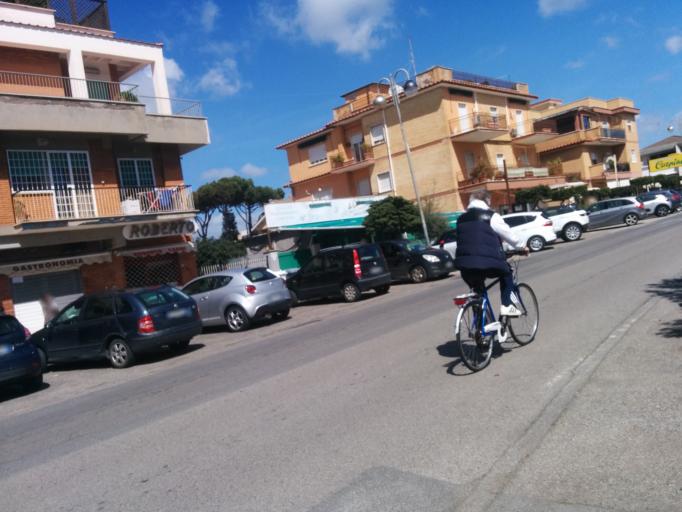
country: IT
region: Latium
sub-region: Citta metropolitana di Roma Capitale
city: Lavinio
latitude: 41.4999
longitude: 12.5890
